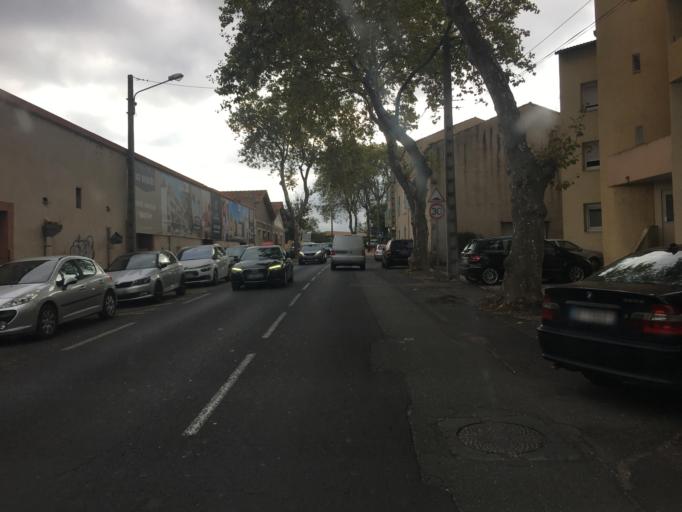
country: FR
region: Languedoc-Roussillon
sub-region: Departement de l'Herault
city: Nebian
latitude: 43.6243
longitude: 3.4349
